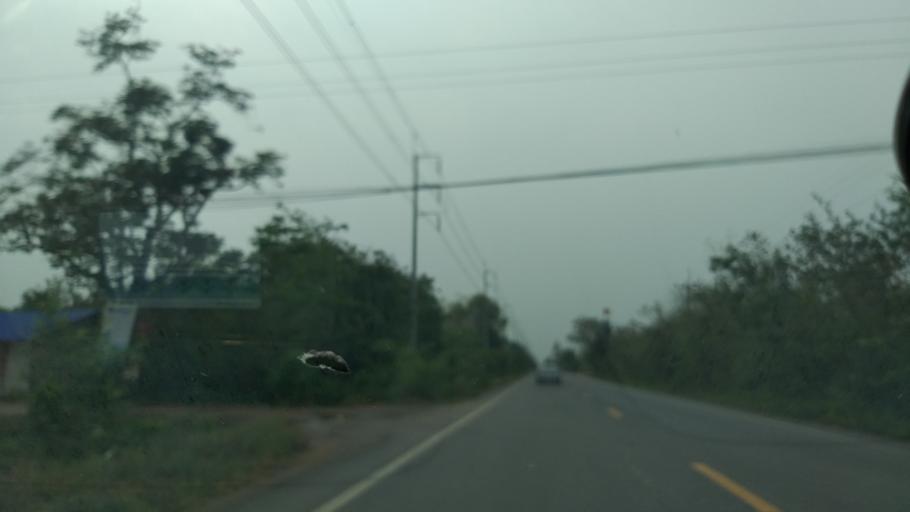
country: TH
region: Chachoengsao
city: Plaeng Yao
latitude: 13.5802
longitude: 101.2328
